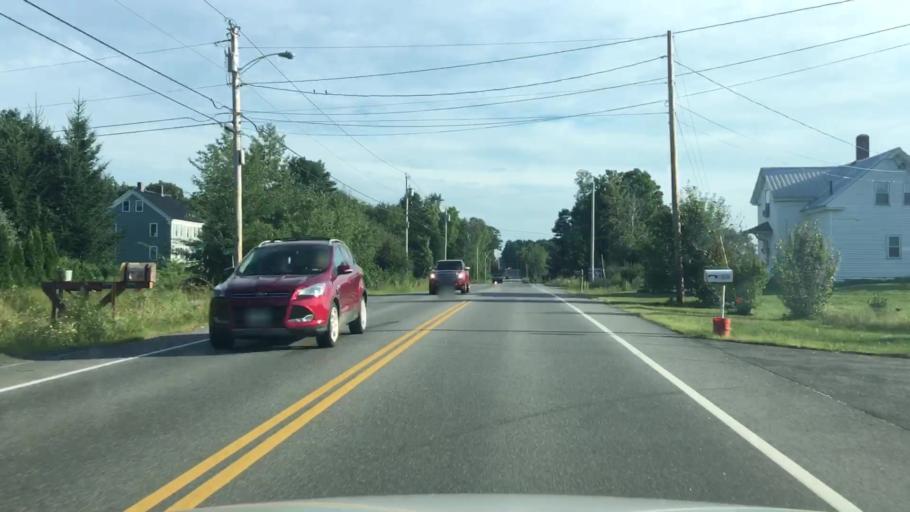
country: US
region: Maine
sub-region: Cumberland County
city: South Windham
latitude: 43.7806
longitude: -70.4397
